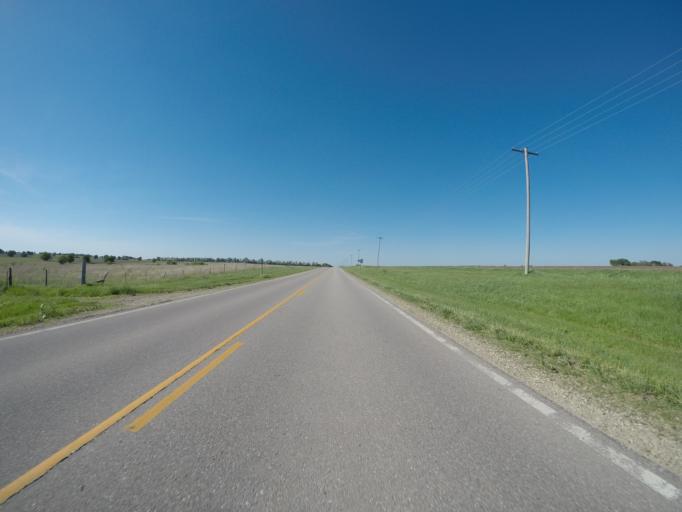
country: US
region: Kansas
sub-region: Riley County
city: Fort Riley North
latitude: 39.3553
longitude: -96.8304
